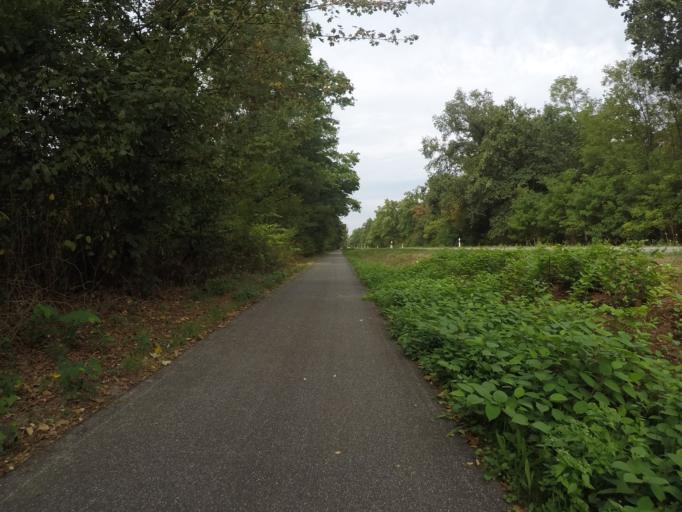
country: DE
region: Rheinland-Pfalz
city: Hanhofen
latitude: 49.3552
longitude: 8.3351
